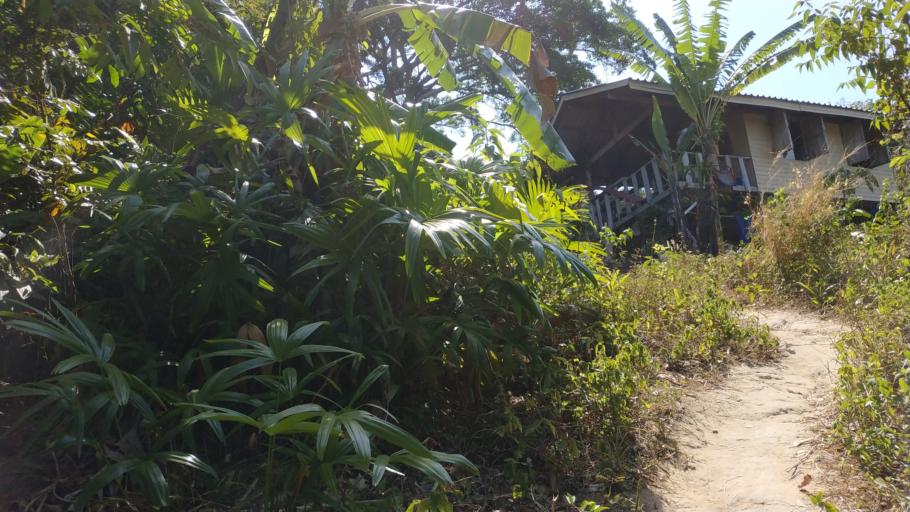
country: TH
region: Phuket
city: Patong
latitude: 7.8737
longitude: 98.2775
